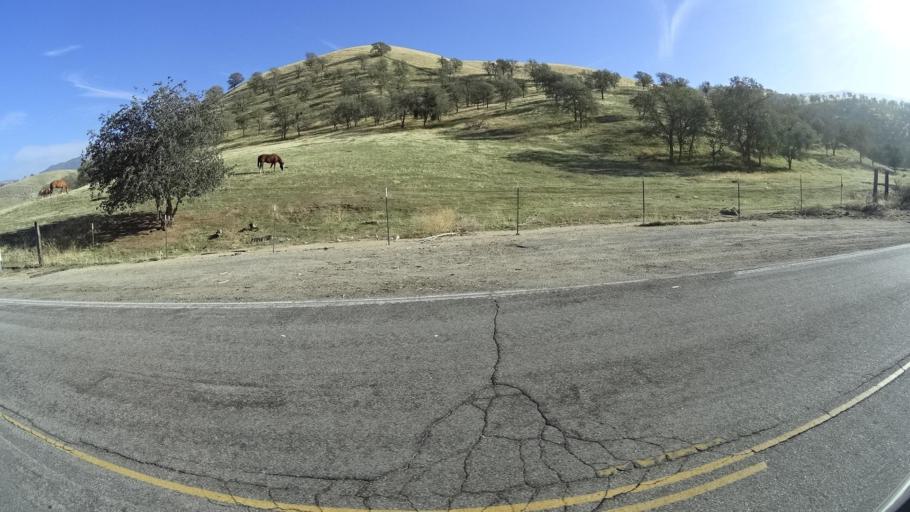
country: US
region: California
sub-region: Kern County
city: Bear Valley Springs
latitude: 35.2693
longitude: -118.6287
